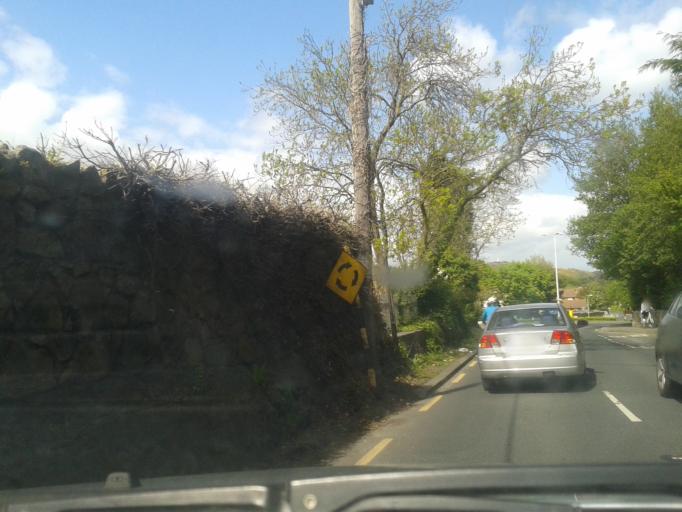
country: IE
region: Leinster
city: Loughlinstown
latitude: 53.2439
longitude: -6.1217
